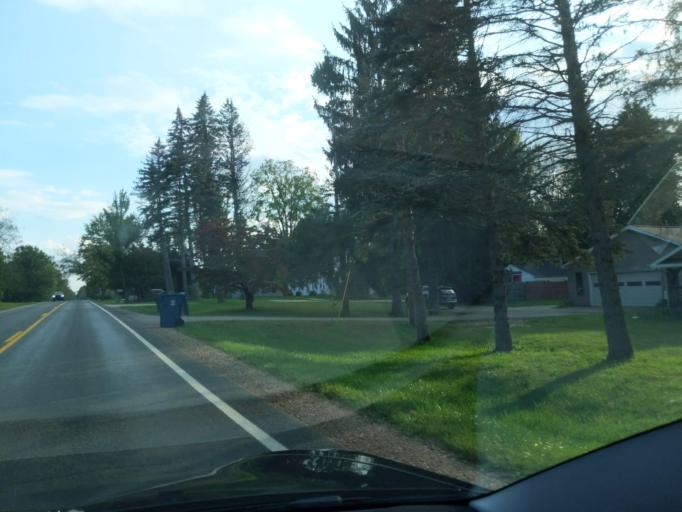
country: US
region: Michigan
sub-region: Jackson County
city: Jackson
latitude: 42.3120
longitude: -84.4628
